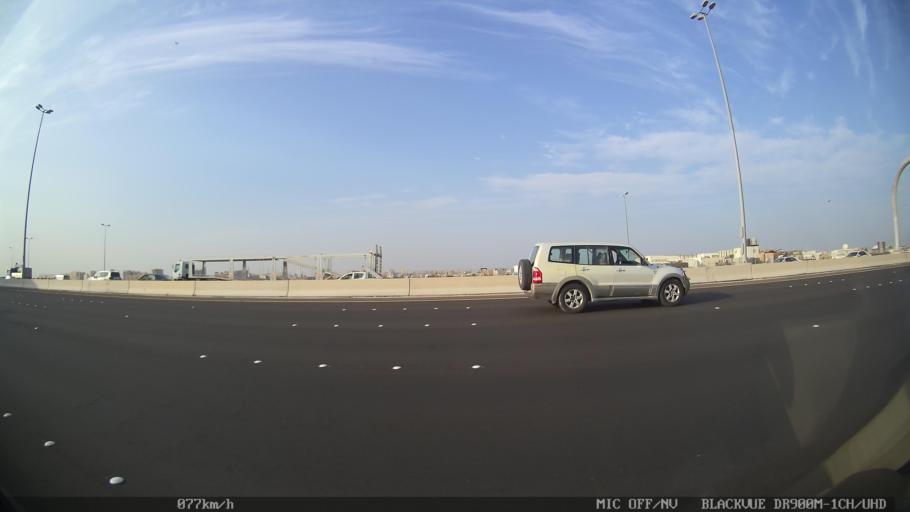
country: KW
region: Al Farwaniyah
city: Janub as Surrah
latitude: 29.2604
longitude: 47.9788
